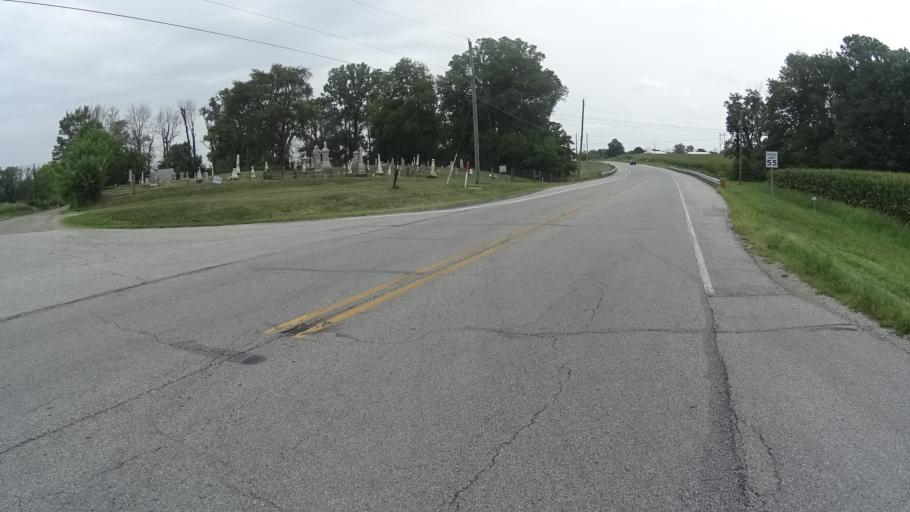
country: US
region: Indiana
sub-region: Madison County
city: Lapel
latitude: 40.0838
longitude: -85.8297
